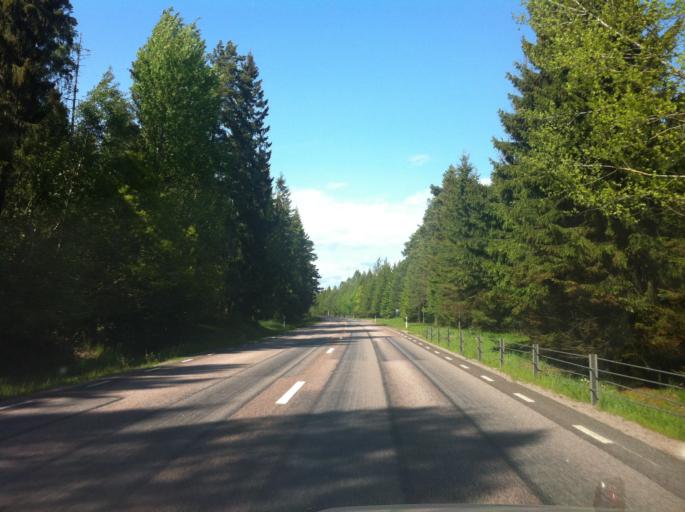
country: SE
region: Vaestra Goetaland
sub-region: Gullspangs Kommun
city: Gullspang
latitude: 59.0742
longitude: 14.1556
